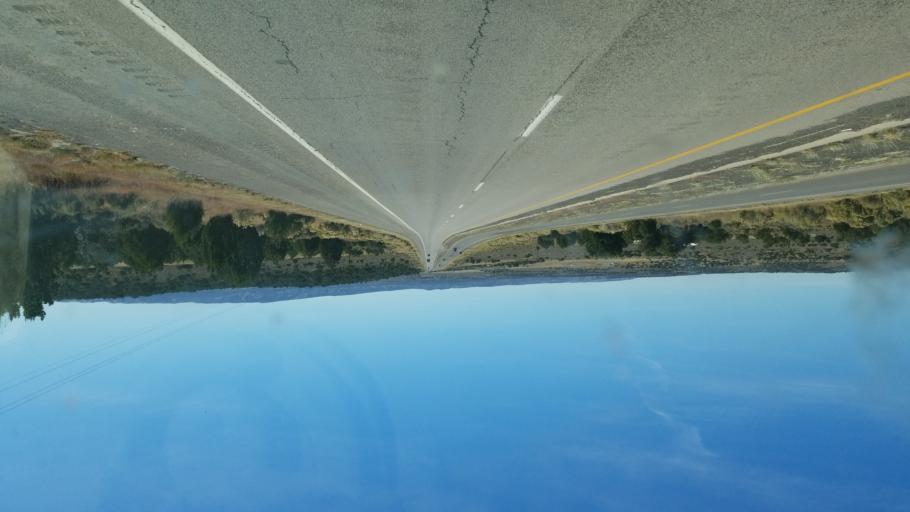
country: US
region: New Mexico
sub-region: McKinley County
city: Twin Lakes
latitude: 35.6357
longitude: -108.8648
